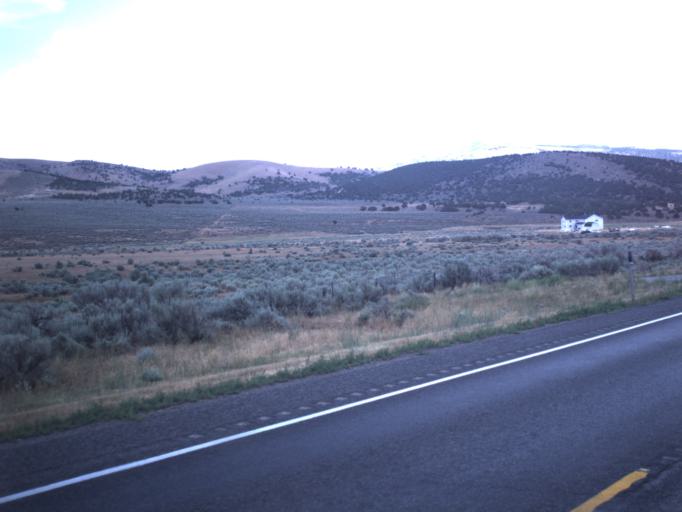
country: US
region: Utah
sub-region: Sanpete County
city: Fountain Green
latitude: 39.6476
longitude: -111.6442
